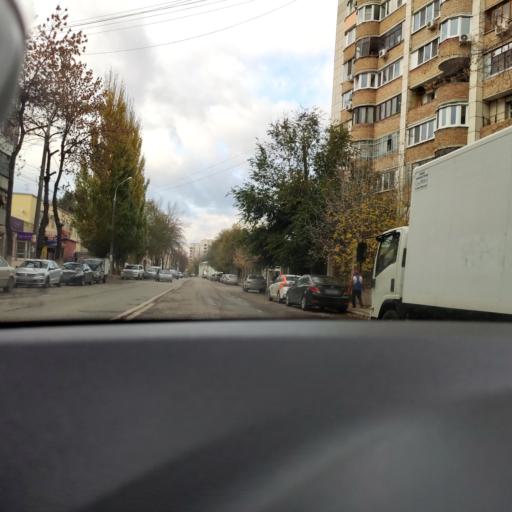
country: RU
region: Samara
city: Petra-Dubrava
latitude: 53.2312
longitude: 50.2777
